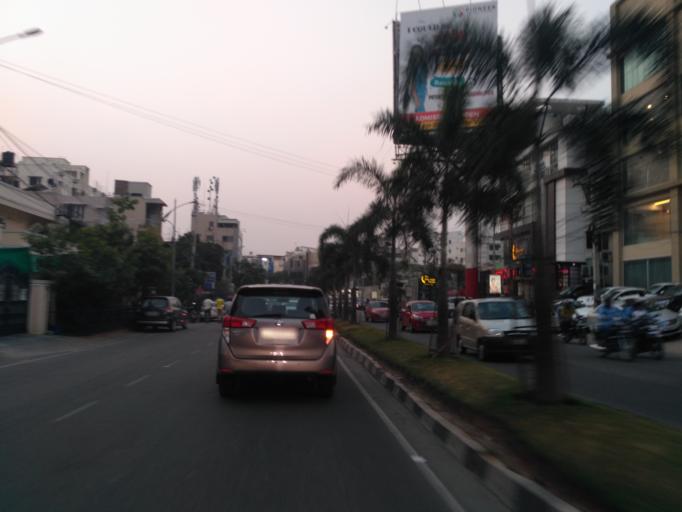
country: IN
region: Telangana
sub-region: Rangareddi
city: Kukatpalli
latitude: 17.4404
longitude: 78.3981
